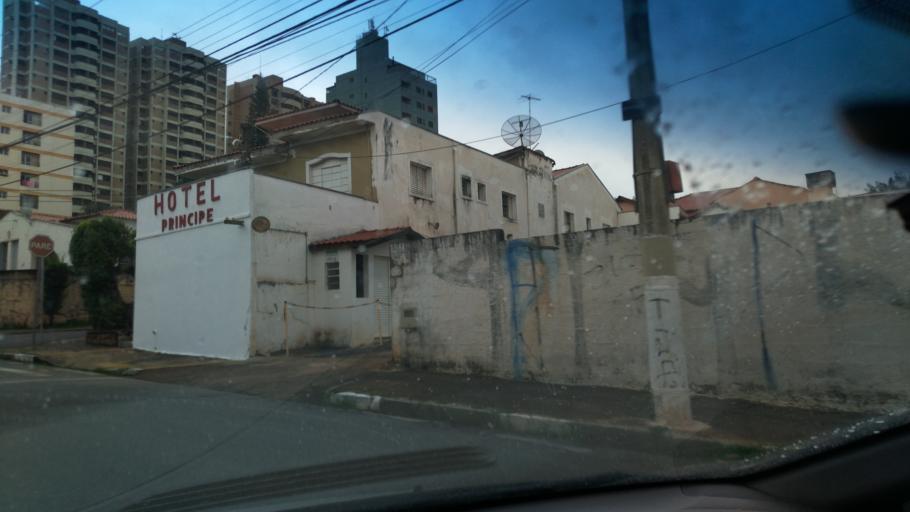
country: BR
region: Sao Paulo
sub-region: Campinas
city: Campinas
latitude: -22.9121
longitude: -47.0507
